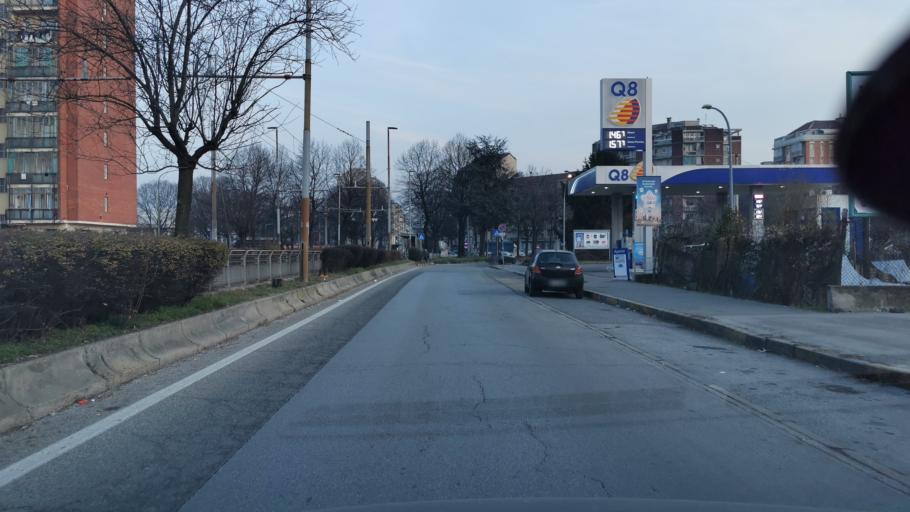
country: IT
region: Piedmont
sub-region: Provincia di Torino
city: Venaria Reale
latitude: 45.0973
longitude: 7.6561
